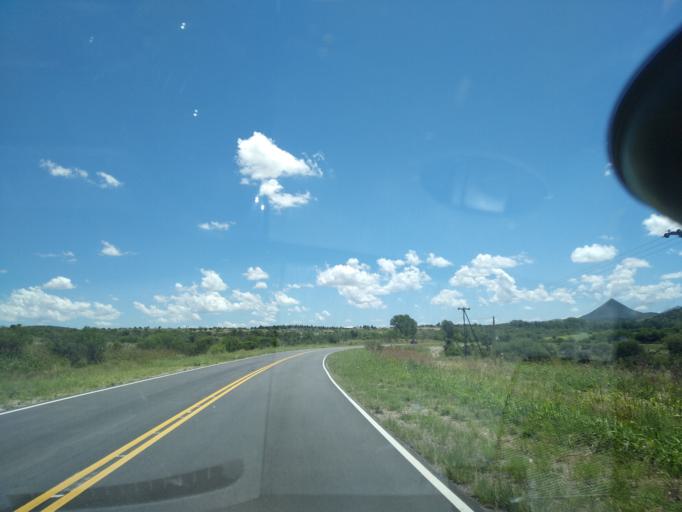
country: AR
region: Cordoba
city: Salsacate
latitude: -31.3501
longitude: -65.0867
